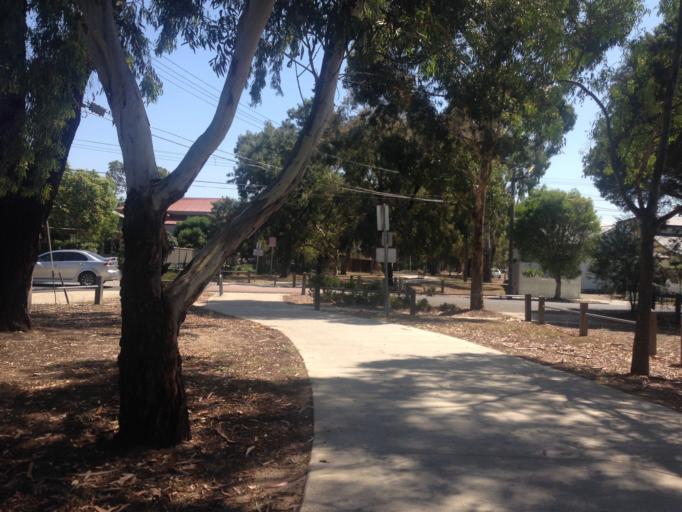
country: AU
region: Victoria
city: Thornbury
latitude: -37.7550
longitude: 144.9887
